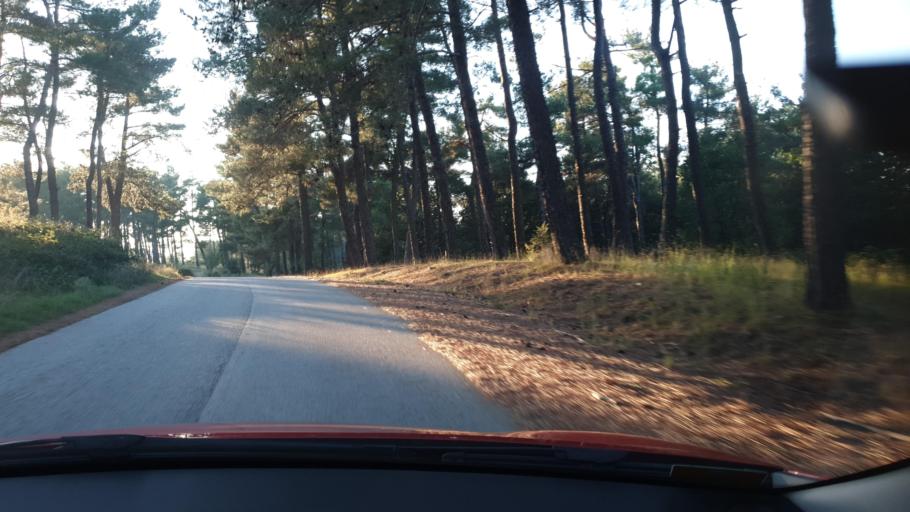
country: GR
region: Central Macedonia
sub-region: Nomos Thessalonikis
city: Peristera
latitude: 40.5114
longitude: 23.2187
